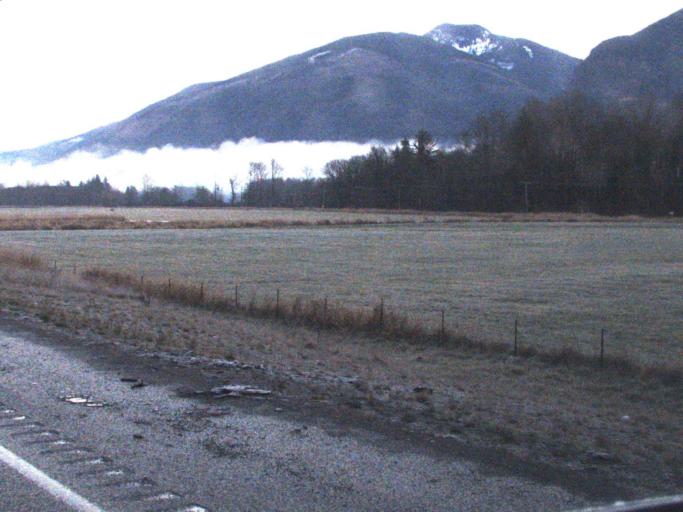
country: US
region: Washington
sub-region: Skagit County
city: Sedro-Woolley
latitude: 48.5302
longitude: -122.0244
